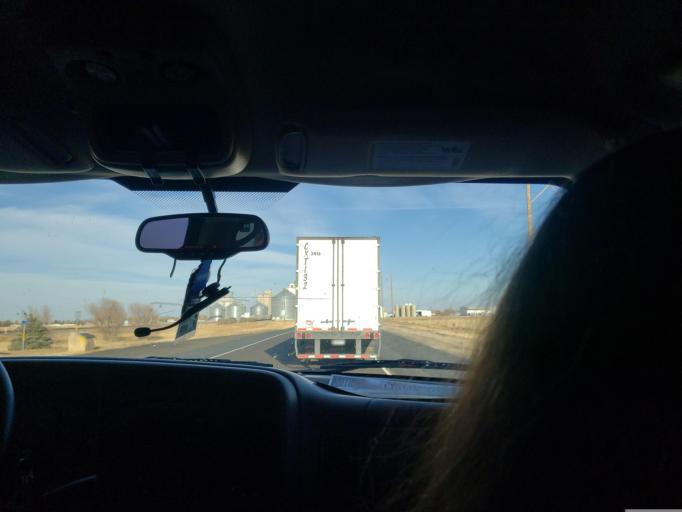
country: US
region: Oklahoma
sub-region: Texas County
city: Goodwell
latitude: 36.4936
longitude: -101.7983
